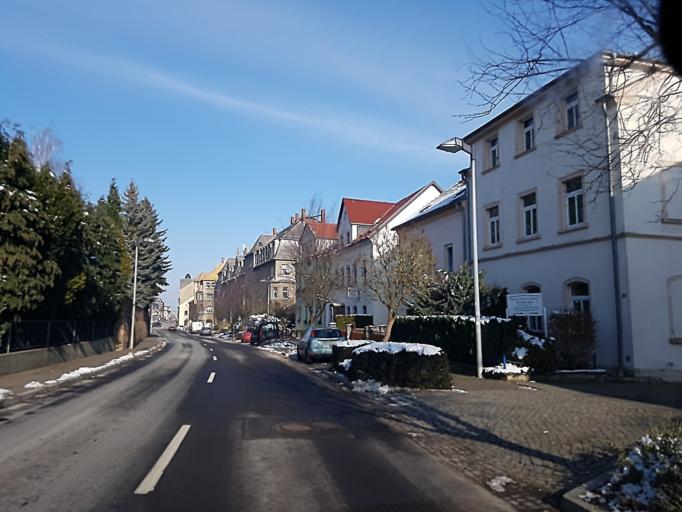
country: DE
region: Saxony
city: Leisnig
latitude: 51.1548
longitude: 12.9277
